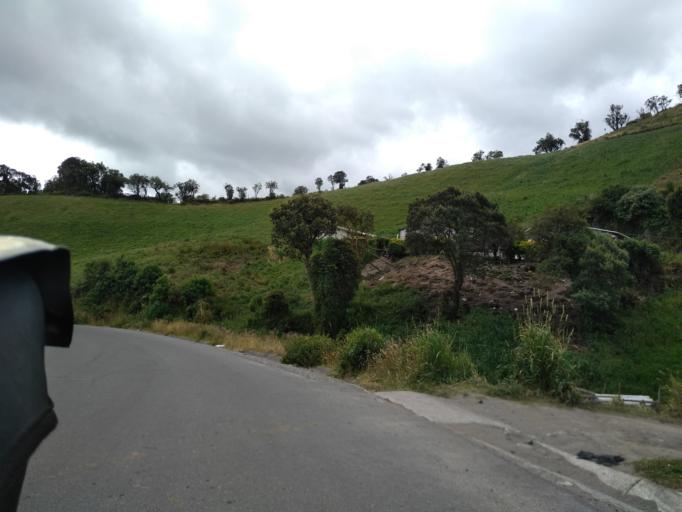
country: EC
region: Cotopaxi
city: Saquisili
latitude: -0.7274
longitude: -78.7533
